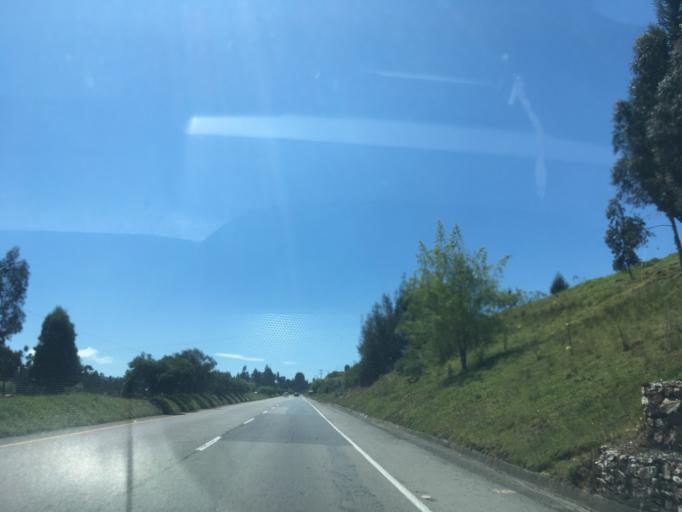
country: CO
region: Boyaca
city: Tuta
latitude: 5.7043
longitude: -73.2454
